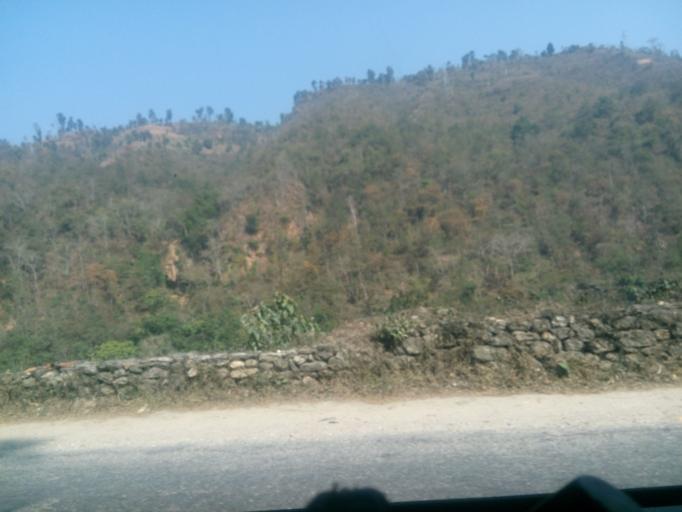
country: NP
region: Central Region
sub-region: Narayani Zone
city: Hitura
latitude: 27.8081
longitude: 84.8886
